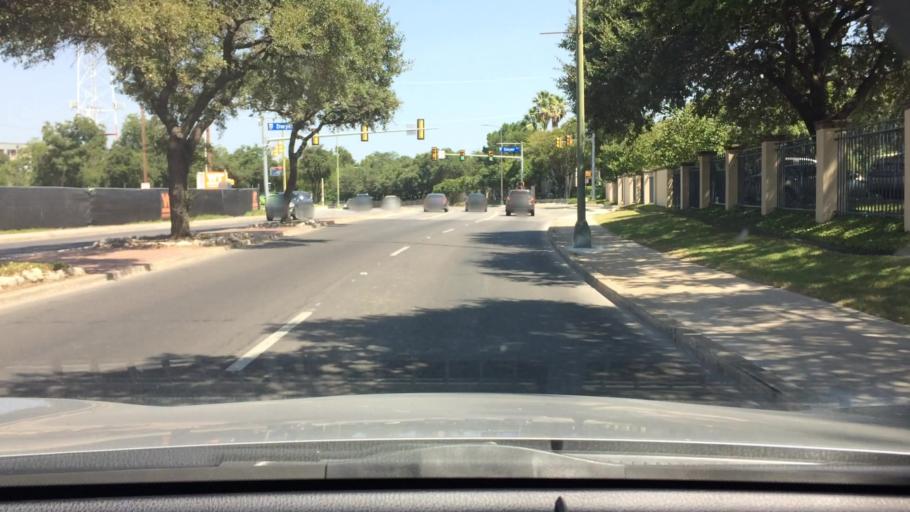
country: US
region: Texas
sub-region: Bexar County
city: San Antonio
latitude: 29.4192
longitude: -98.4950
